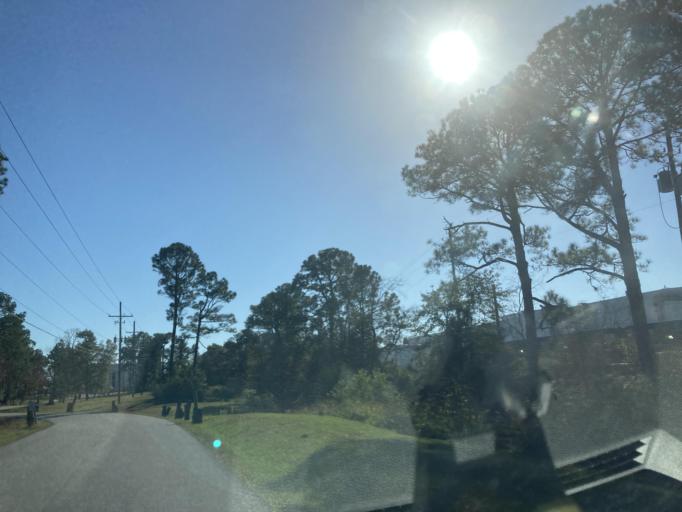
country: US
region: Mississippi
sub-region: Harrison County
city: West Gulfport
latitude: 30.4320
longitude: -89.0614
